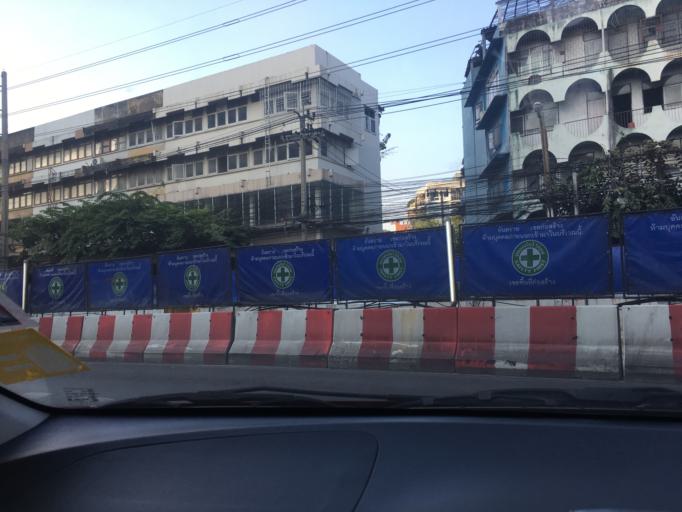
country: TH
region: Bangkok
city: Huai Khwang
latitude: 13.8035
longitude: 100.5783
